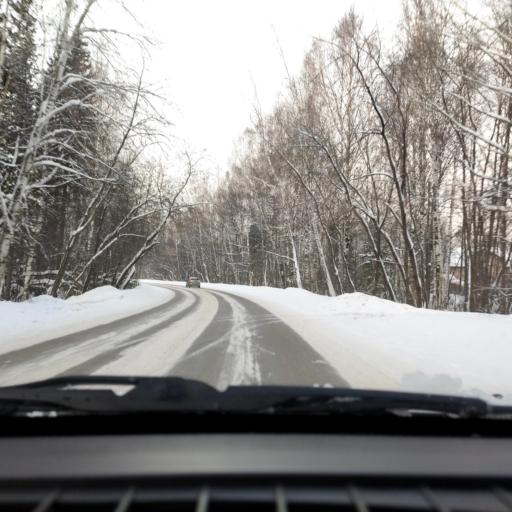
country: RU
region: Perm
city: Overyata
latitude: 58.0530
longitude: 55.8840
